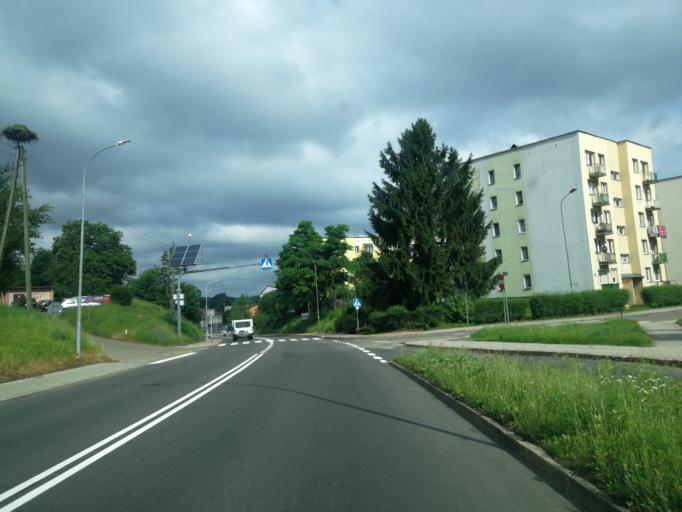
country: PL
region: Subcarpathian Voivodeship
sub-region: Powiat leski
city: Lesko
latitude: 49.4660
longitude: 22.3356
